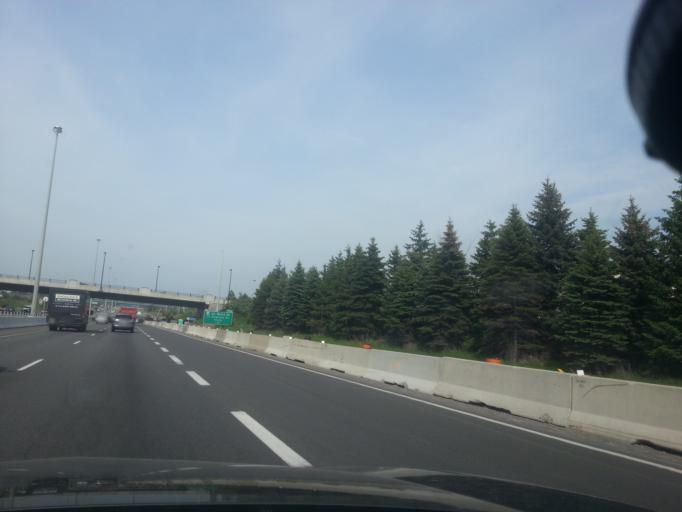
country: CA
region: Ontario
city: Bells Corners
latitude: 45.3099
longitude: -75.9041
